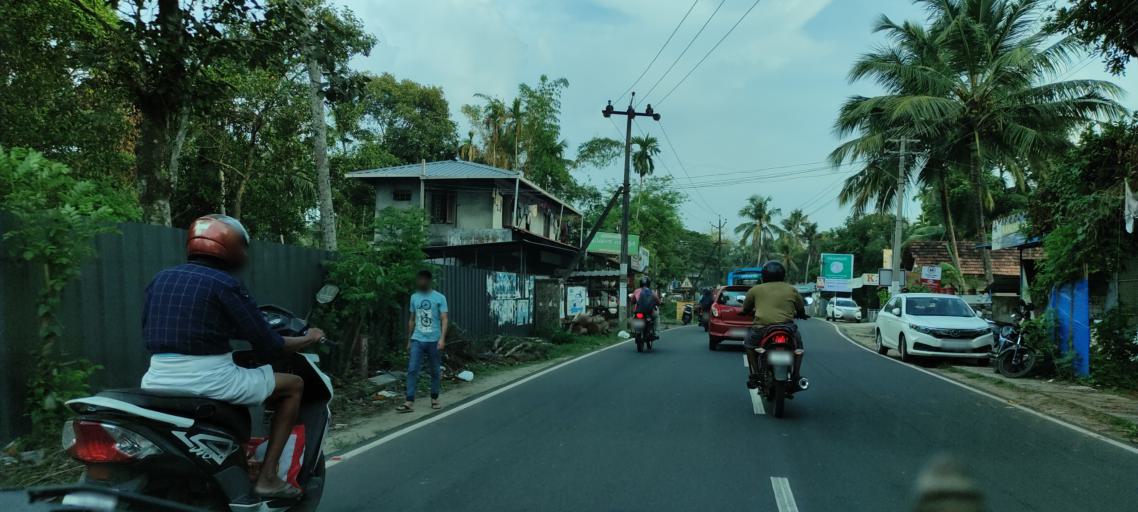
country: IN
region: Kerala
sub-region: Alappuzha
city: Arukutti
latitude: 9.8488
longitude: 76.3286
